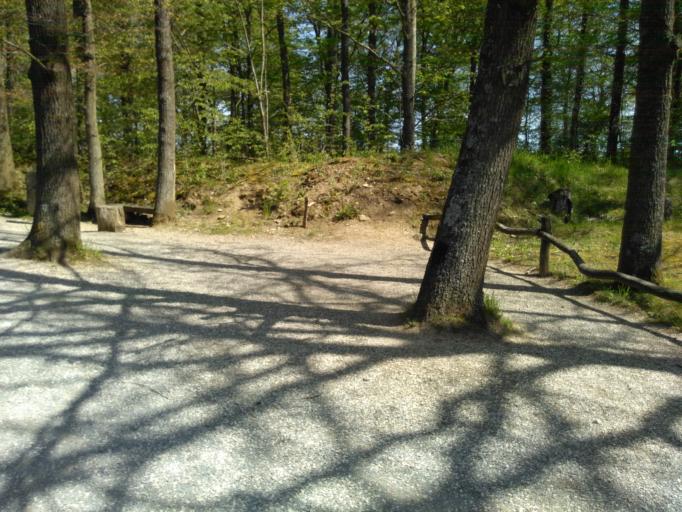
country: DE
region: Baden-Wuerttemberg
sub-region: Regierungsbezirk Stuttgart
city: Igersheim
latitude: 49.4691
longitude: 9.7969
